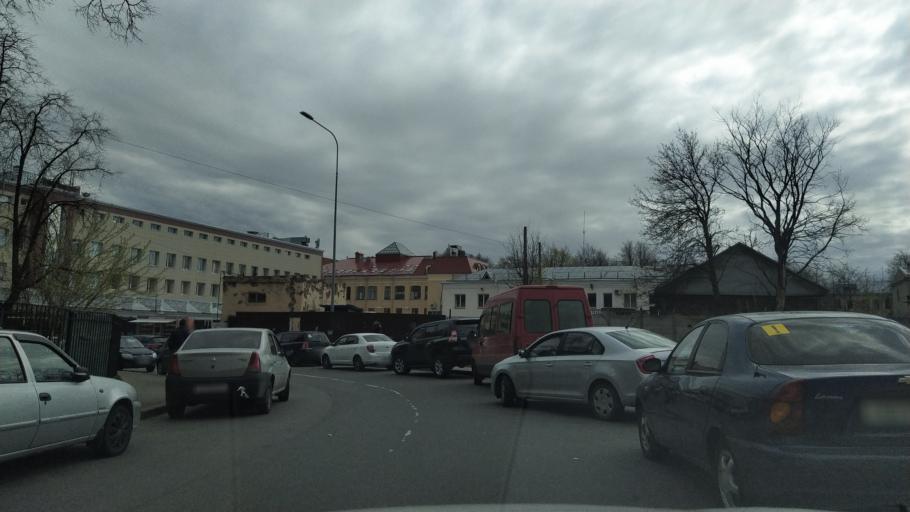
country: RU
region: St.-Petersburg
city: Centralniy
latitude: 59.9394
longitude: 30.3920
